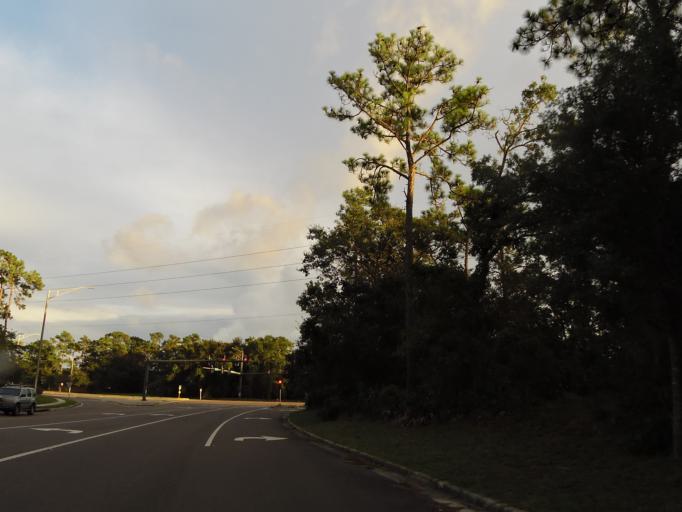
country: US
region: Florida
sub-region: Duval County
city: Atlantic Beach
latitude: 30.3599
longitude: -81.4809
